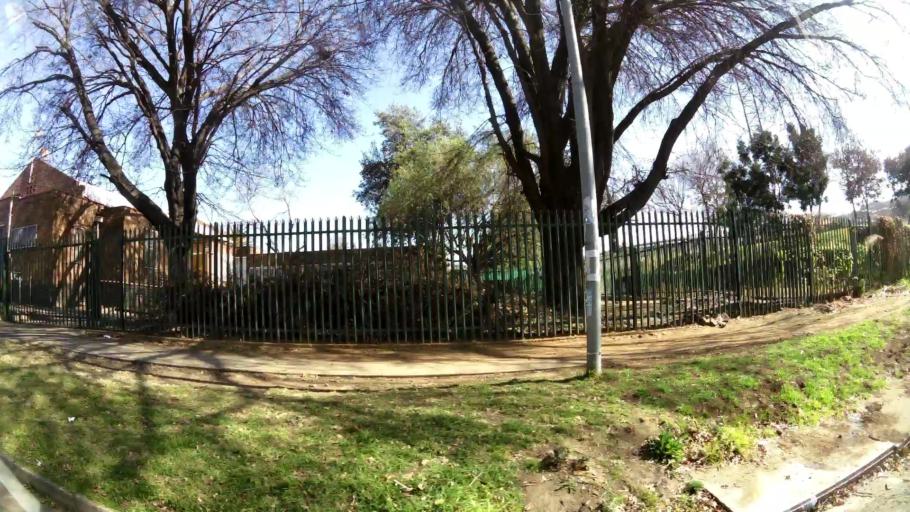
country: ZA
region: Gauteng
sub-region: City of Johannesburg Metropolitan Municipality
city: Johannesburg
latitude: -26.1944
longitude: 28.0677
